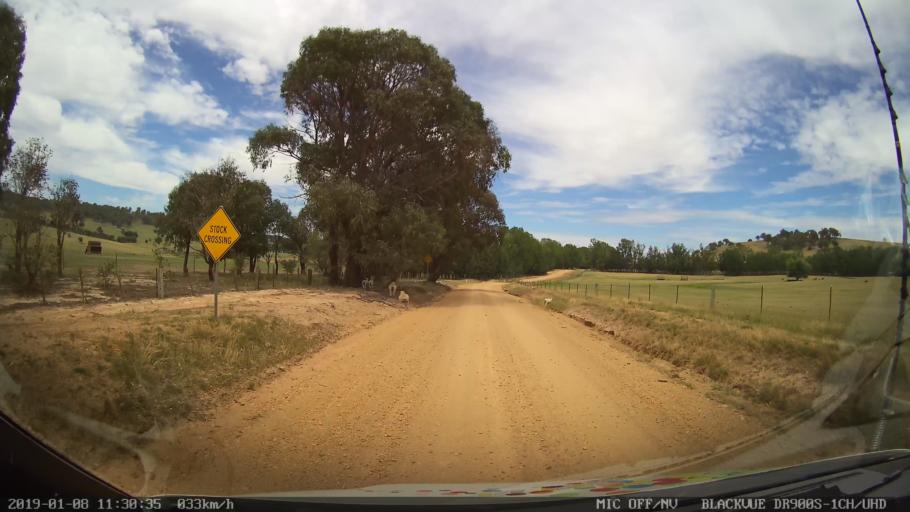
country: AU
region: New South Wales
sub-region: Guyra
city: Guyra
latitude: -30.3089
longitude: 151.5432
